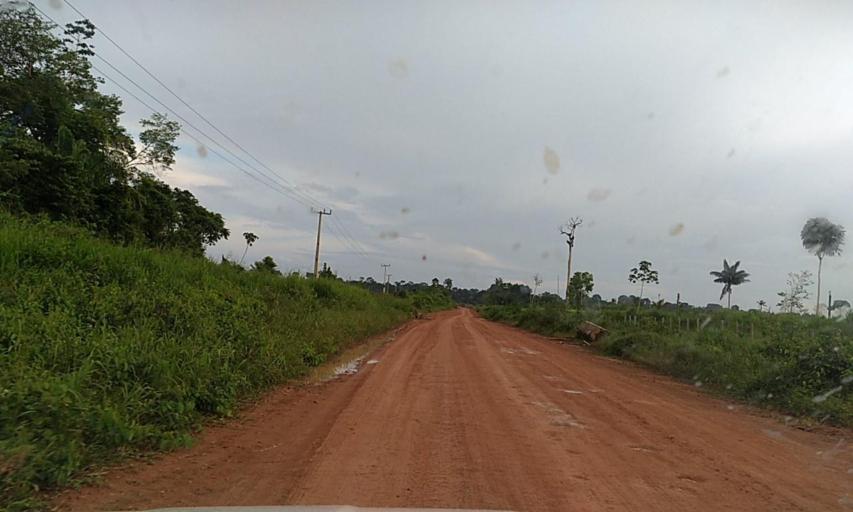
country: BR
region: Para
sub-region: Senador Jose Porfirio
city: Senador Jose Porfirio
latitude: -2.6902
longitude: -51.8260
